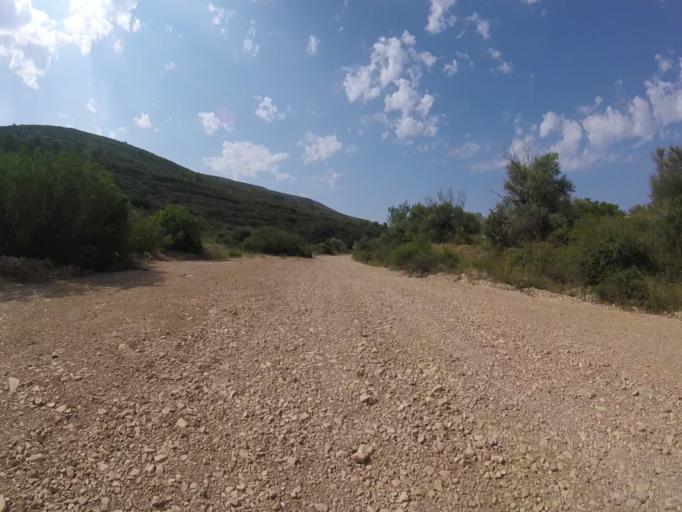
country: ES
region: Valencia
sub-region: Provincia de Castello
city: Alcala de Xivert
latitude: 40.3302
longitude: 0.1938
